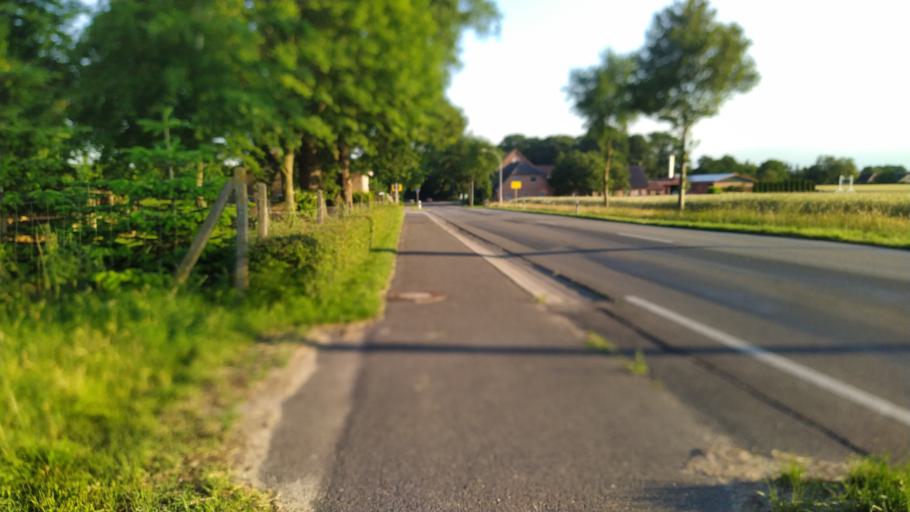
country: DE
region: Lower Saxony
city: Ebersdorf
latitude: 53.5304
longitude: 9.0527
